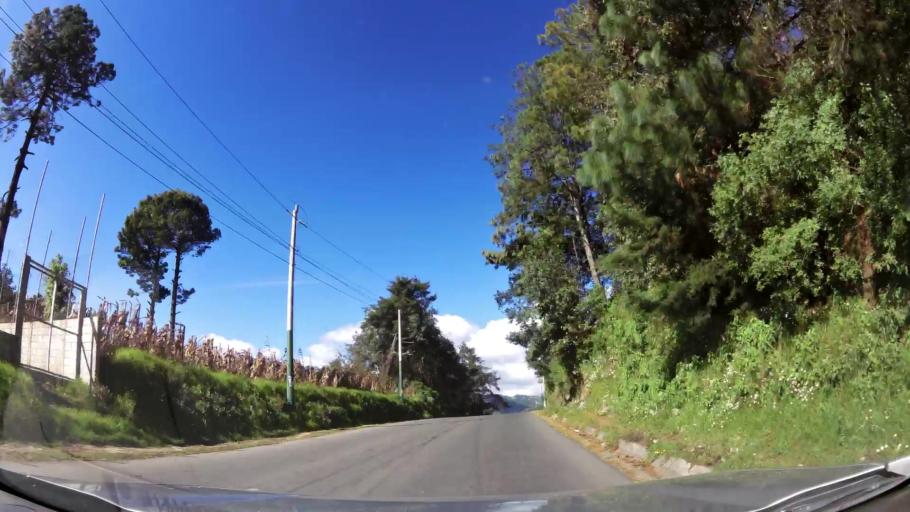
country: GT
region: Solola
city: Solola
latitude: 14.8079
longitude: -91.1797
